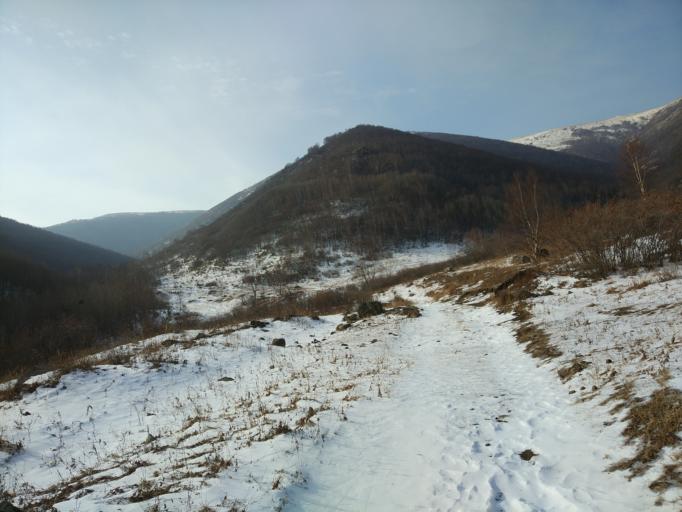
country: CN
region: Hebei
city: Xiwanzi
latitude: 40.8402
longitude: 115.4572
